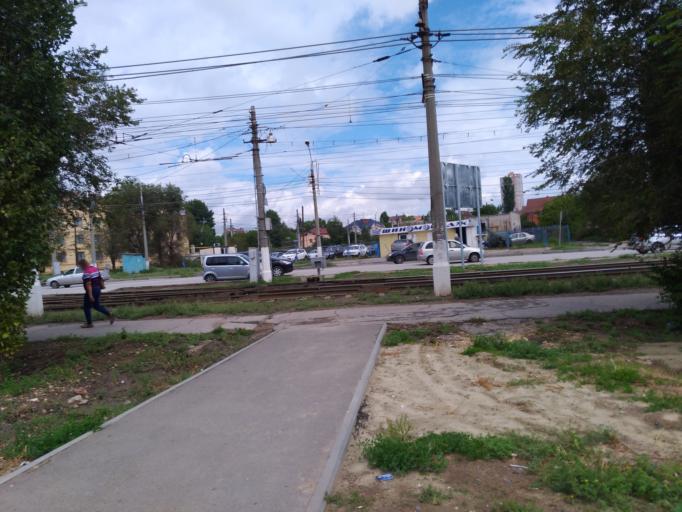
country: RU
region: Volgograd
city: Volgograd
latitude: 48.7142
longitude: 44.4953
